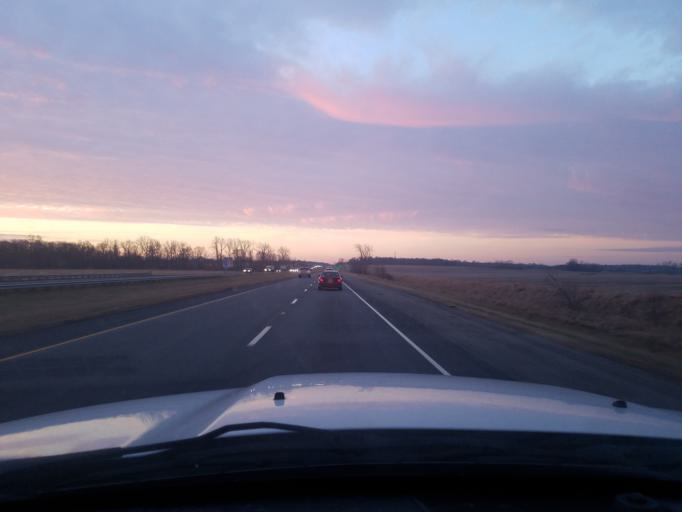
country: US
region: Indiana
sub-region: Huntington County
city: Roanoke
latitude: 41.0088
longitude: -85.2588
